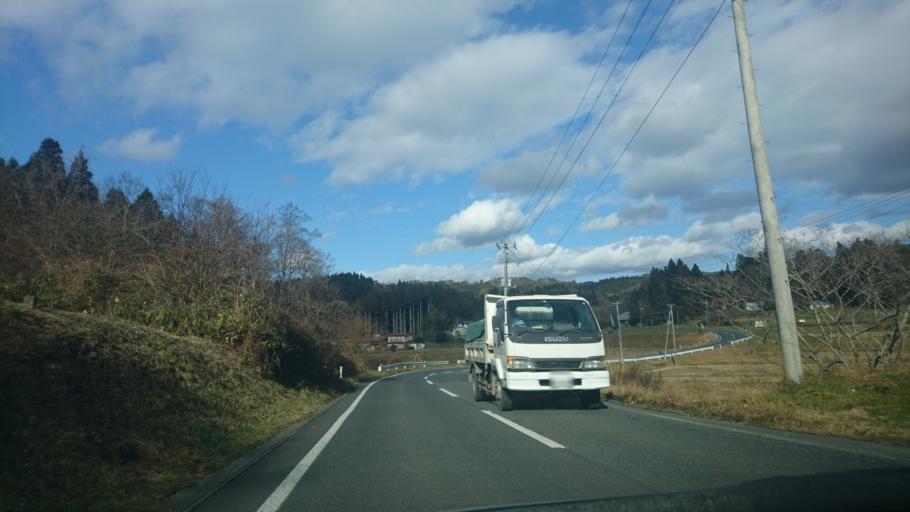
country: JP
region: Iwate
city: Ichinoseki
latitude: 38.9454
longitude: 141.4064
